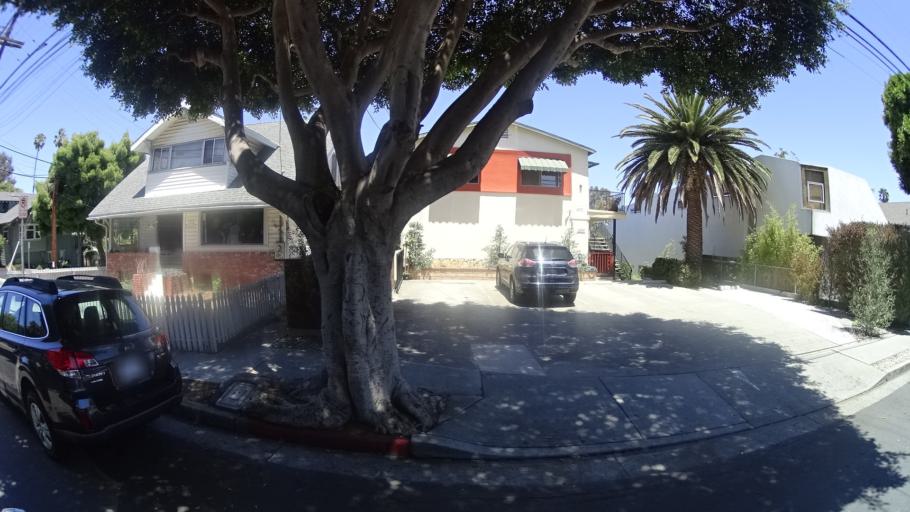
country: US
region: California
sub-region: Los Angeles County
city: Santa Monica
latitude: 34.0039
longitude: -118.4748
